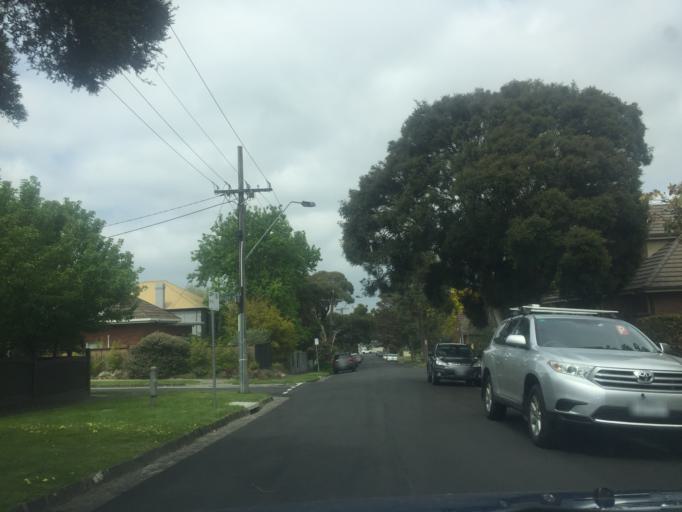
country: AU
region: Victoria
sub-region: Boroondara
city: Kew
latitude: -37.8124
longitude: 145.0359
